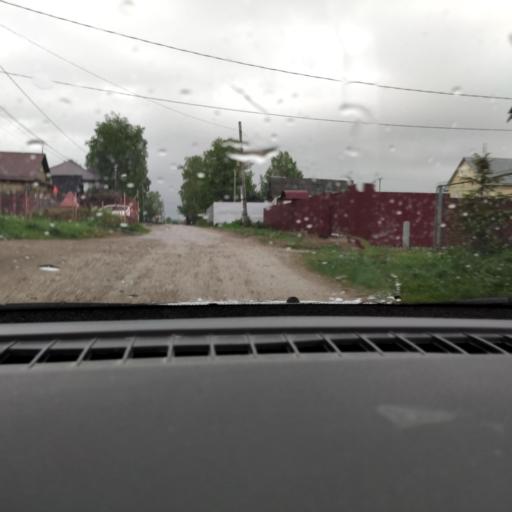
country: RU
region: Perm
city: Kondratovo
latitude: 58.0516
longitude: 56.0253
